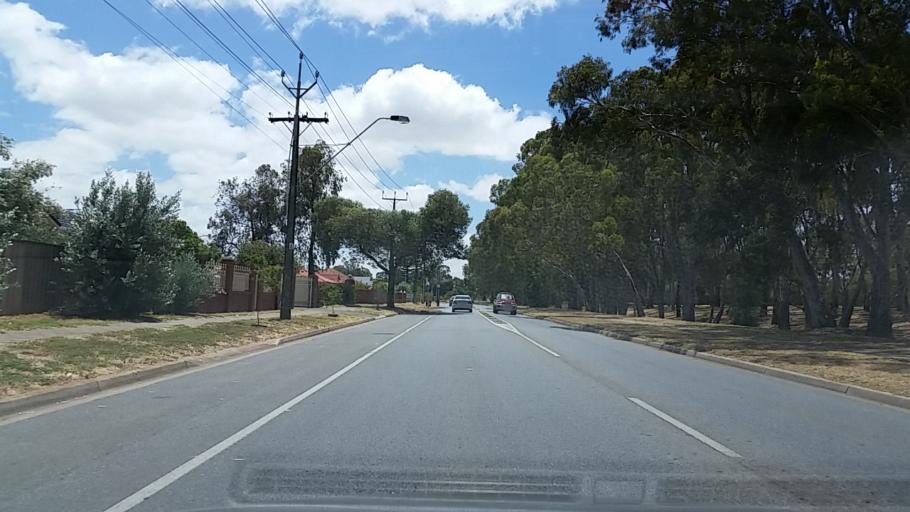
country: AU
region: South Australia
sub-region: Salisbury
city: Salisbury
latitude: -34.7714
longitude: 138.6175
